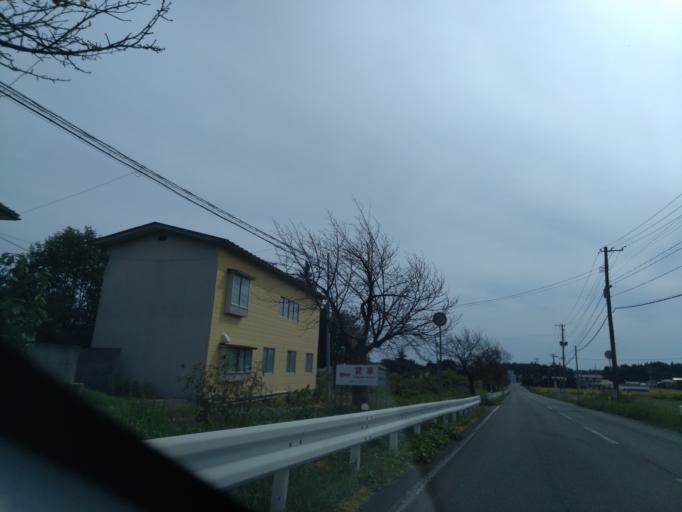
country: JP
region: Iwate
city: Hanamaki
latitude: 39.4299
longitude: 141.0841
